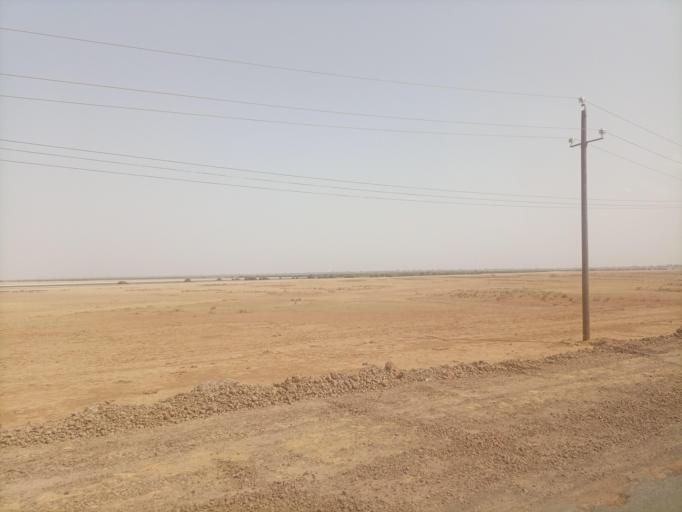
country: SN
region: Fatick
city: Foundiougne
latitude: 14.1525
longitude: -16.4707
